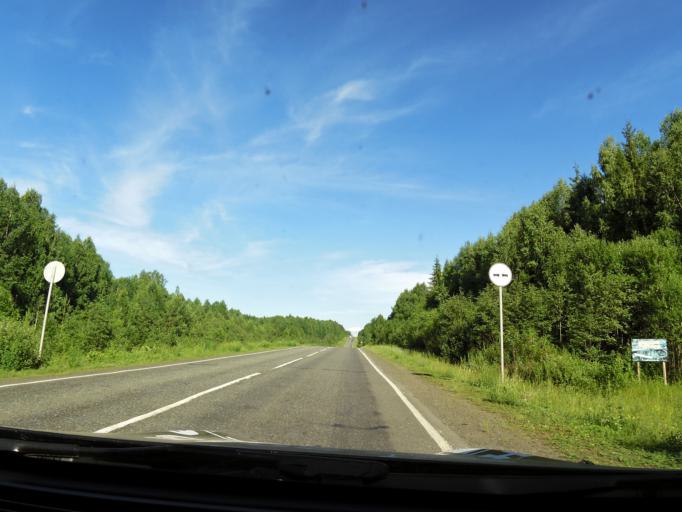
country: RU
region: Kirov
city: Chernaya Kholunitsa
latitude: 58.8897
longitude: 51.3598
